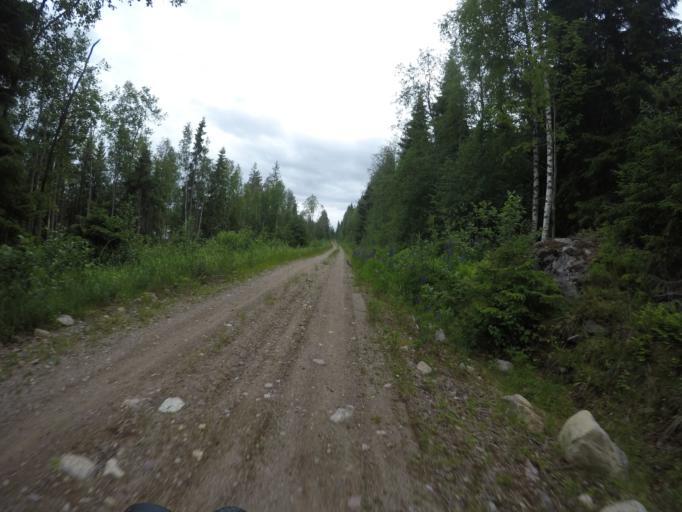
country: SE
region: Dalarna
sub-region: Ludvika Kommun
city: Abborrberget
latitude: 60.0323
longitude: 14.5994
